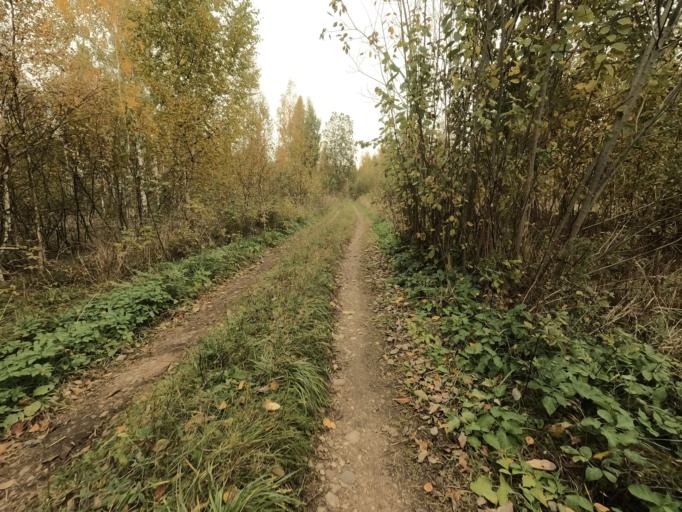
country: RU
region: Novgorod
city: Pankovka
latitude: 58.8711
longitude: 30.9369
